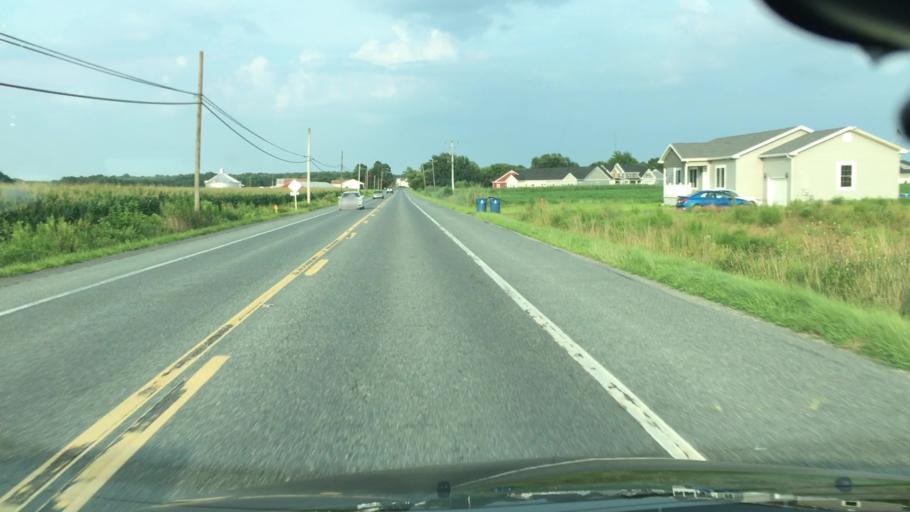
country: US
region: Delaware
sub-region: Sussex County
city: Selbyville
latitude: 38.4642
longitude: -75.1776
